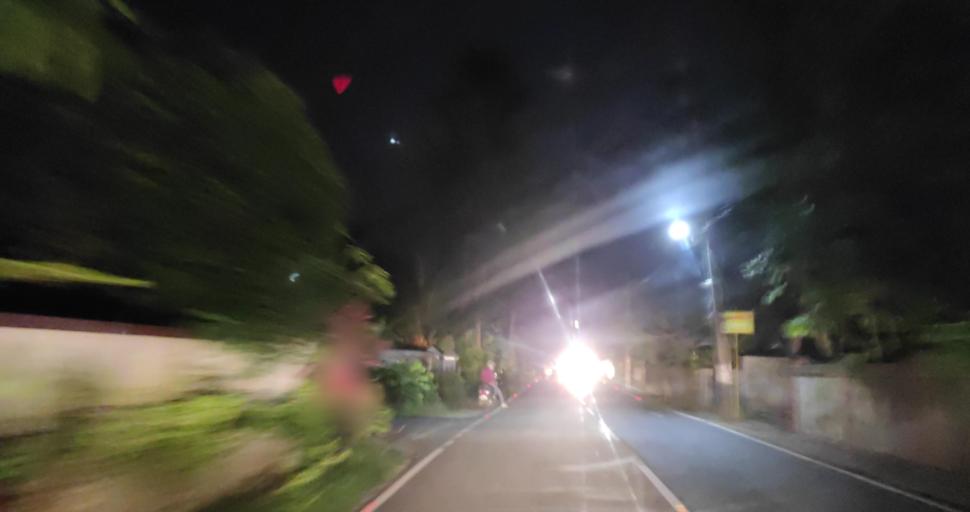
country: IN
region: Kerala
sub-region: Alappuzha
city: Vayalar
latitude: 9.6808
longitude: 76.3227
